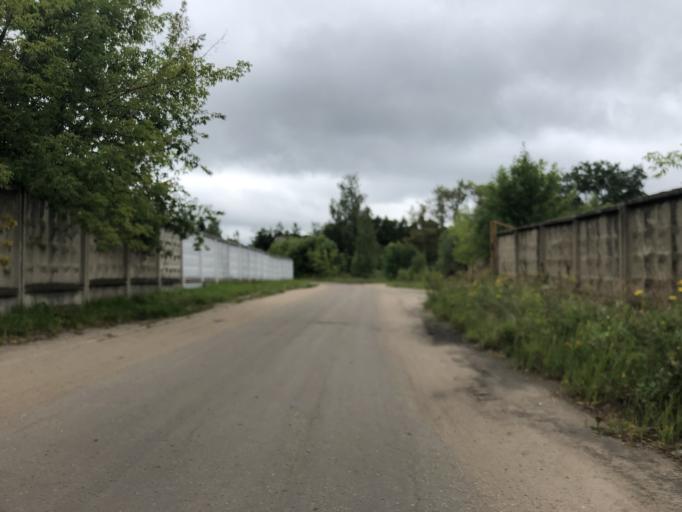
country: RU
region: Tverskaya
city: Rzhev
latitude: 56.2405
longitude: 34.3316
